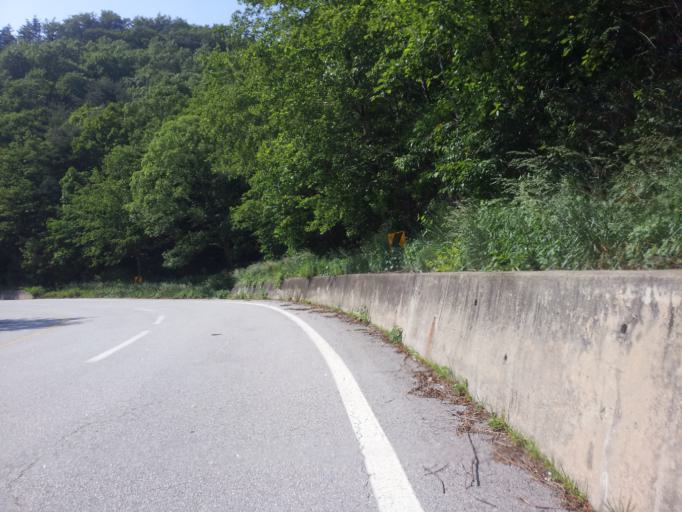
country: KR
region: Chungcheongbuk-do
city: Okcheon
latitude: 36.4795
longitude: 127.6478
